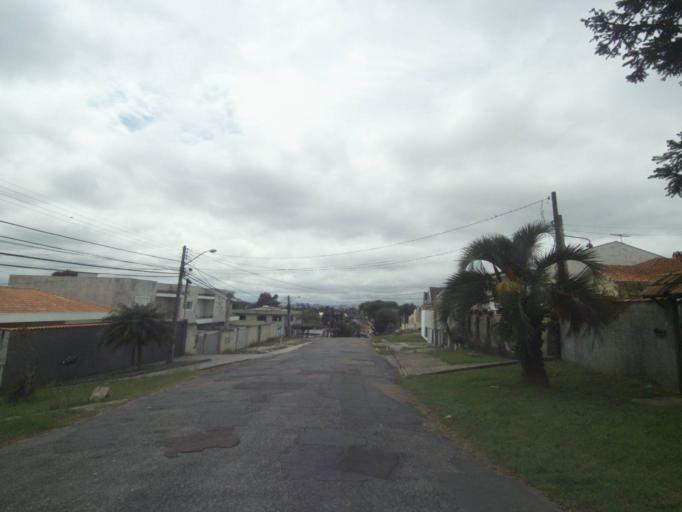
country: BR
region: Parana
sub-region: Curitiba
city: Curitiba
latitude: -25.3878
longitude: -49.2779
